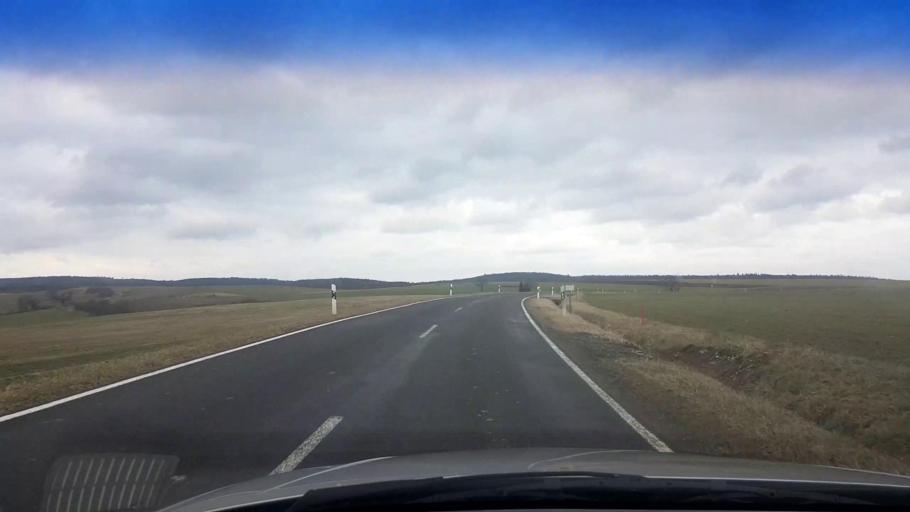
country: DE
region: Bavaria
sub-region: Upper Franconia
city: Priesendorf
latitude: 49.9248
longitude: 10.6877
